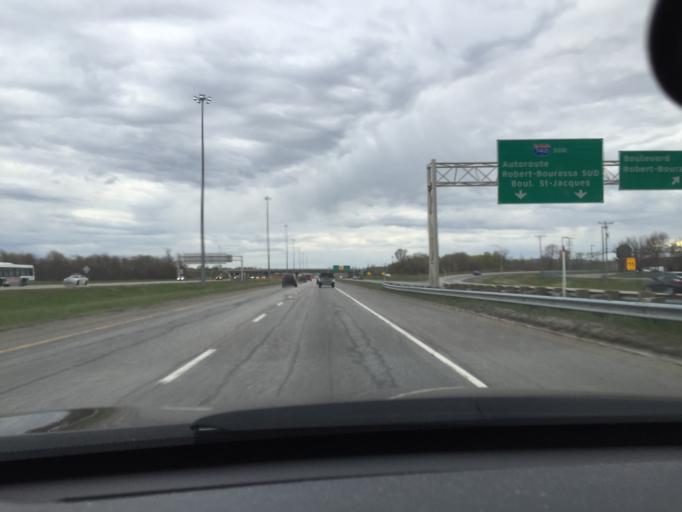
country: CA
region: Quebec
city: L'Ancienne-Lorette
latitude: 46.8265
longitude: -71.2923
